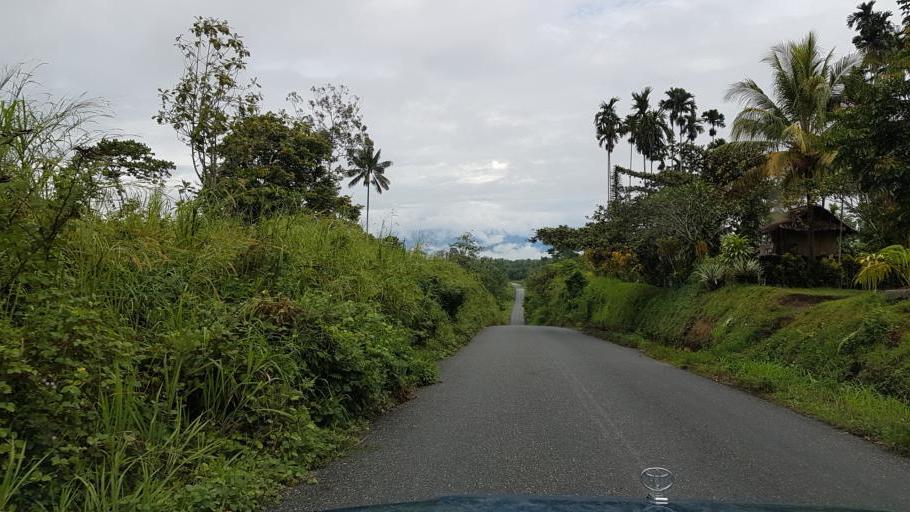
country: PG
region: Northern Province
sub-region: Sohe
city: Popondetta
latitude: -8.8256
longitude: 148.0778
